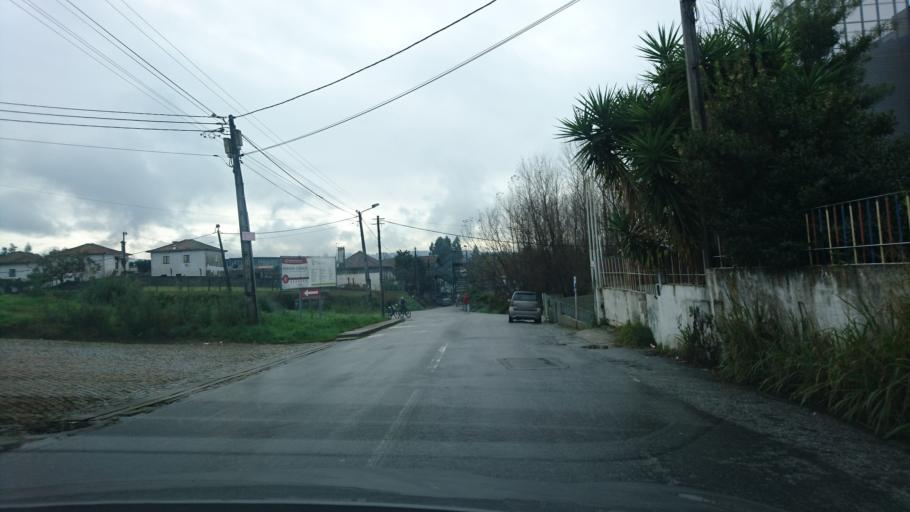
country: PT
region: Porto
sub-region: Paredes
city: Recarei
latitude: 41.1536
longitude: -8.3964
